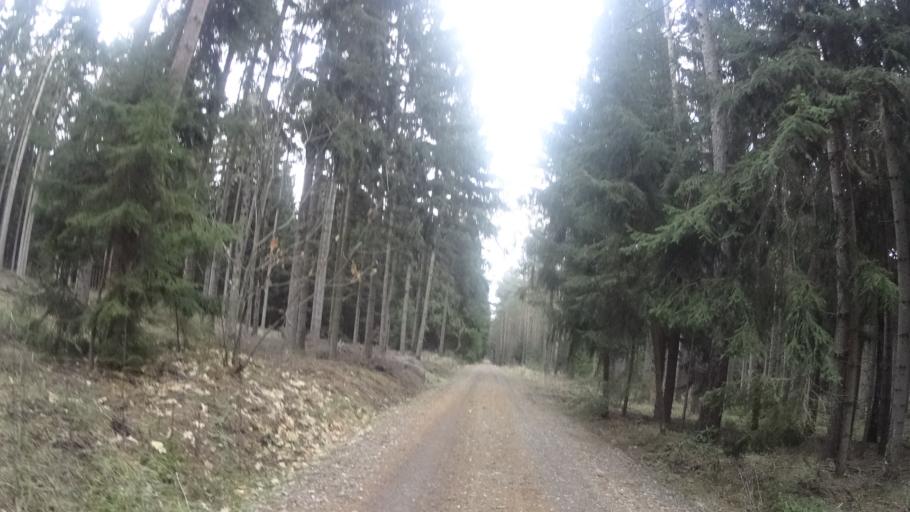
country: DE
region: Thuringia
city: Zeulenroda
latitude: 50.6245
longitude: 12.0007
